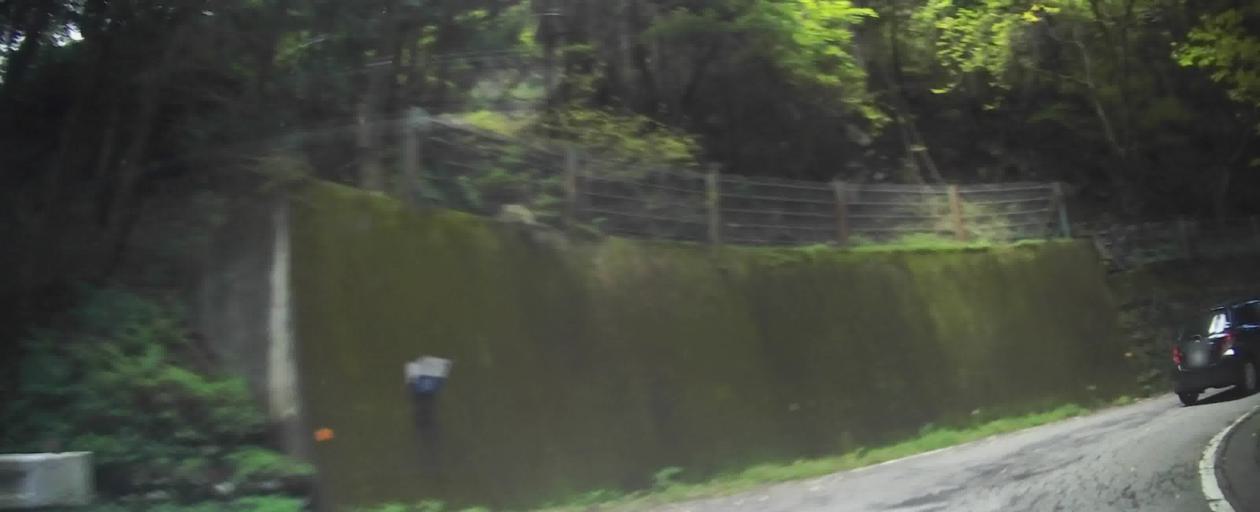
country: JP
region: Gunma
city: Shibukawa
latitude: 36.4576
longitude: 138.8963
